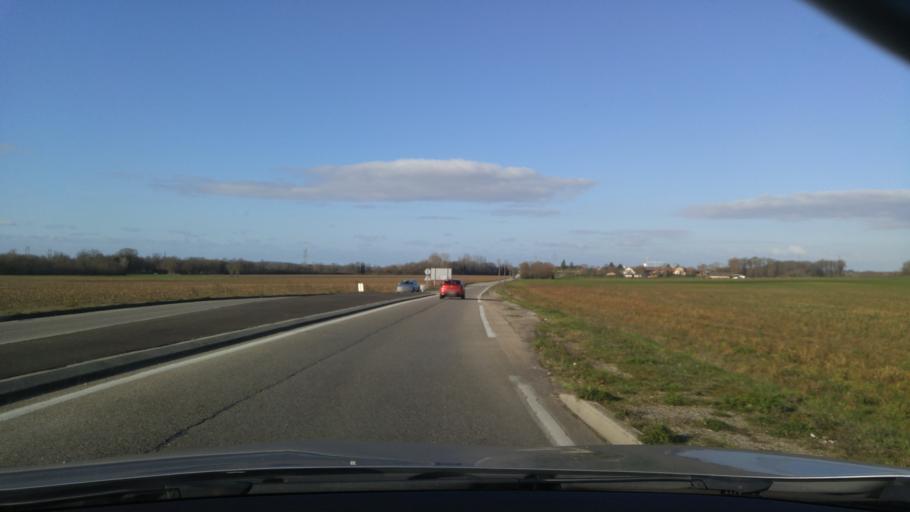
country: FR
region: Rhone-Alpes
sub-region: Departement de l'Isere
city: Villemoirieu
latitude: 45.7054
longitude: 5.1977
